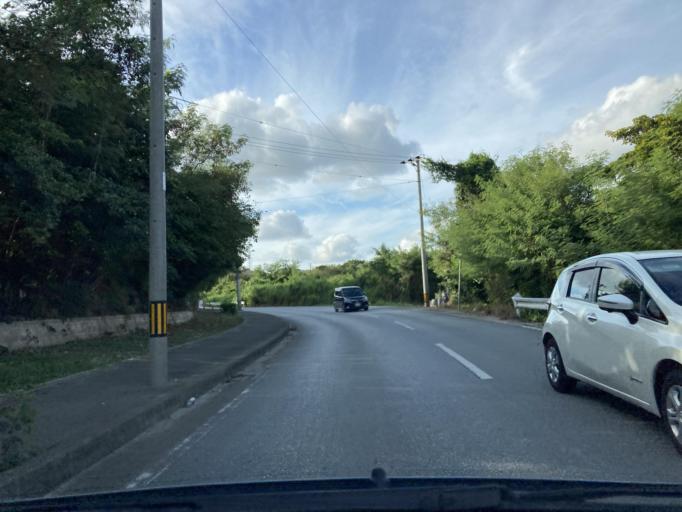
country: JP
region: Okinawa
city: Itoman
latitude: 26.1334
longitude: 127.7522
